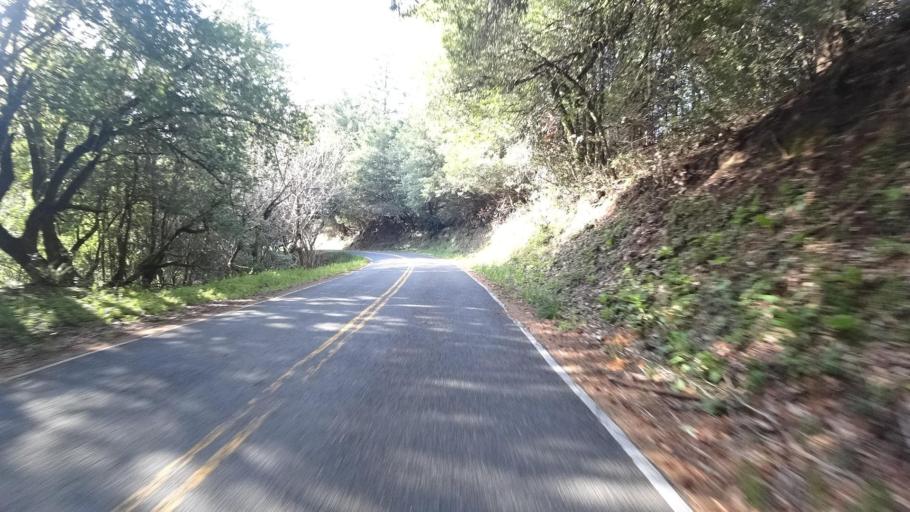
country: US
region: California
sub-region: Humboldt County
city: Blue Lake
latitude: 40.7235
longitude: -123.9445
